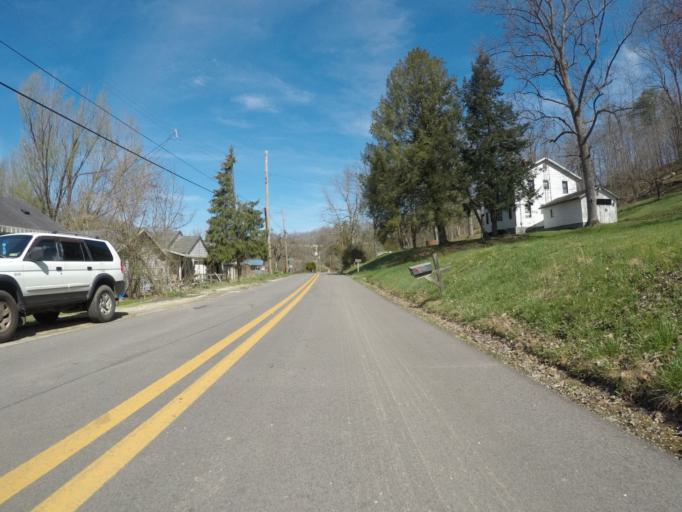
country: US
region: West Virginia
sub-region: Cabell County
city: Pea Ridge
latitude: 38.4050
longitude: -82.3492
